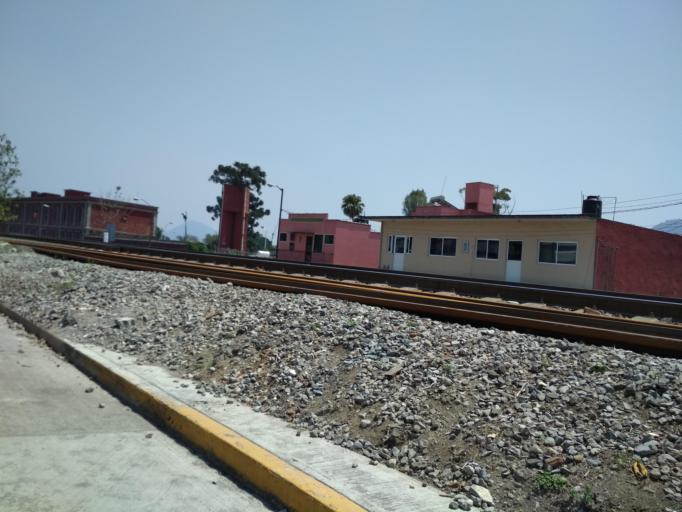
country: MX
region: Veracruz
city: Orizaba
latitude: 18.8482
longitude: -97.0852
